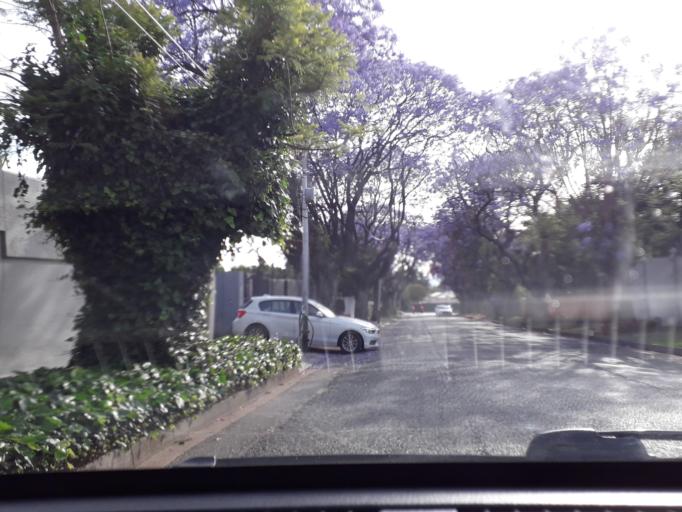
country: ZA
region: Gauteng
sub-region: City of Johannesburg Metropolitan Municipality
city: Johannesburg
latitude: -26.1479
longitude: 28.0943
